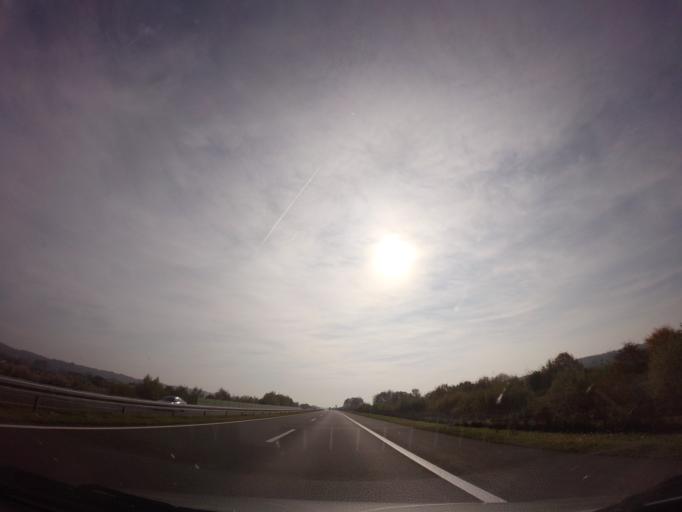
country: HR
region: Varazdinska
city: Remetinec
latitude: 46.0306
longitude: 16.2949
